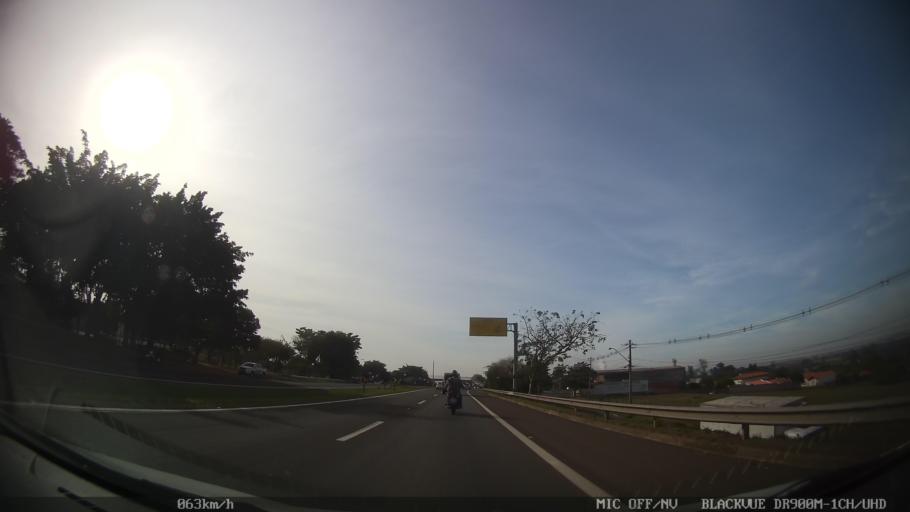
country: BR
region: Sao Paulo
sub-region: Piracicaba
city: Piracicaba
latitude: -22.6800
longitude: -47.7050
